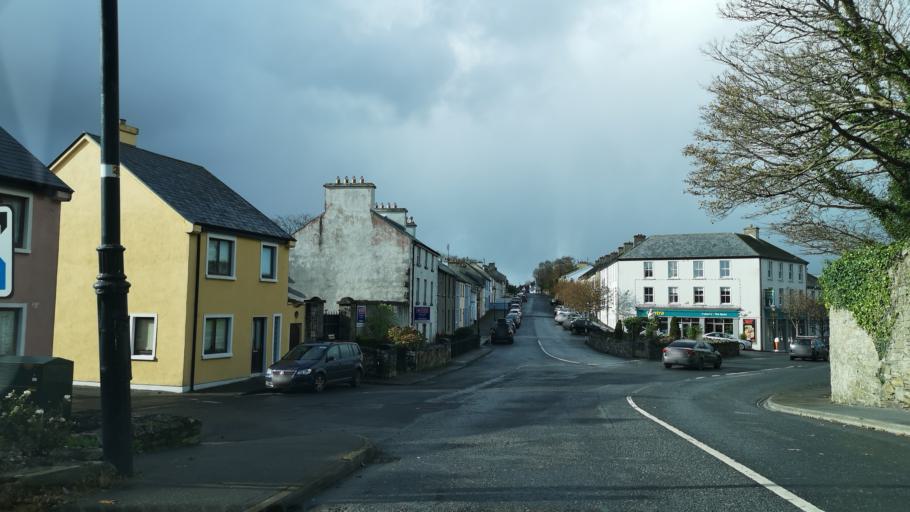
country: IE
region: Connaught
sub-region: Maigh Eo
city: Westport
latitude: 53.7989
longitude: -9.5440
